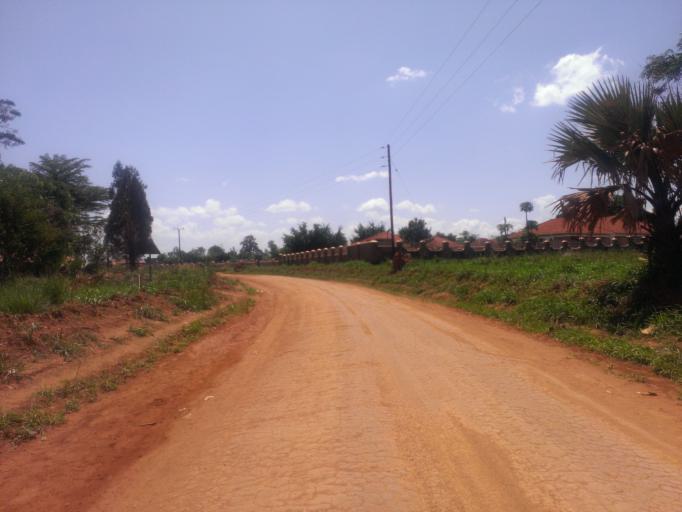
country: UG
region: Northern Region
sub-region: Gulu District
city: Gulu
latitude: 2.7868
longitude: 32.3010
